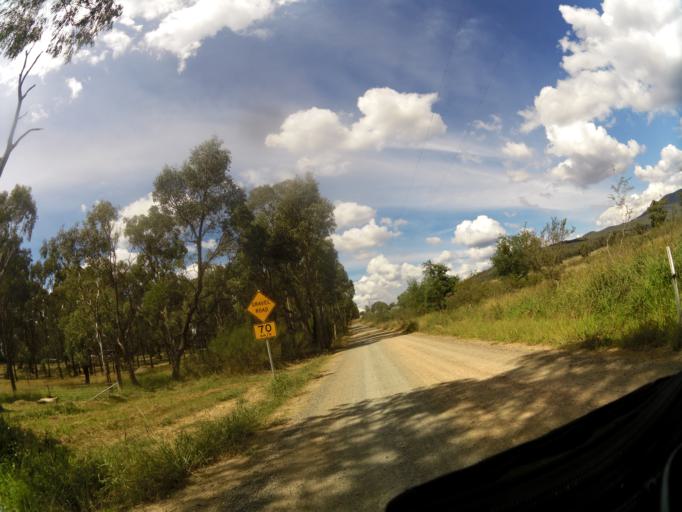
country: AU
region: Victoria
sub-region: Benalla
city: Benalla
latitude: -36.7783
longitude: 145.9744
